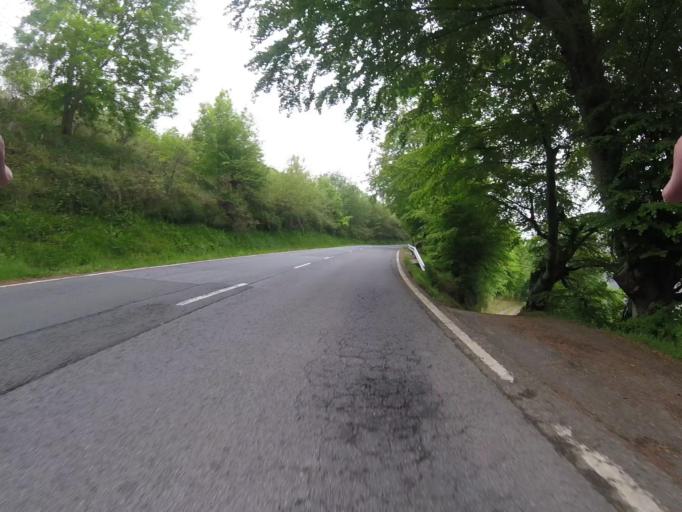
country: ES
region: Navarre
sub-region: Provincia de Navarra
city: Zugarramurdi
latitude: 43.2527
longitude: -1.4832
